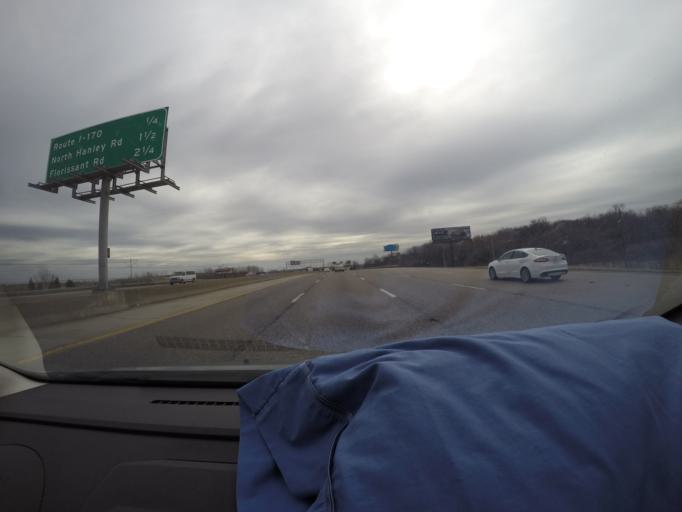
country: US
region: Missouri
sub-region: Saint Louis County
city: Woodson Terrace
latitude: 38.7329
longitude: -90.3428
